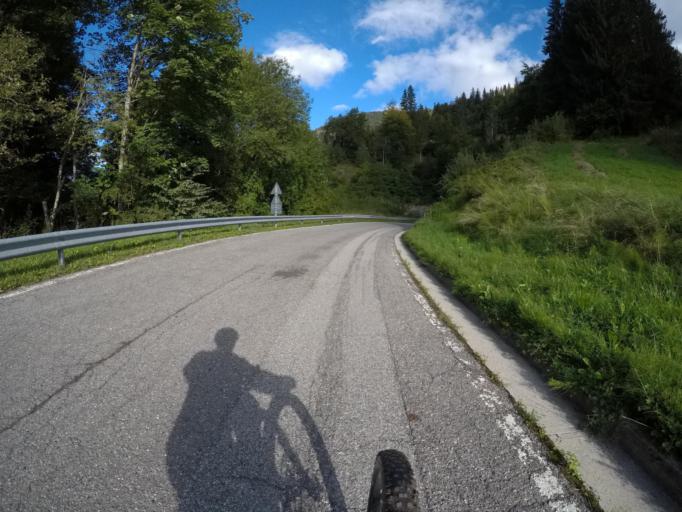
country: IT
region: Friuli Venezia Giulia
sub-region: Provincia di Udine
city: Ligosullo
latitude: 46.5387
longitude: 13.0843
